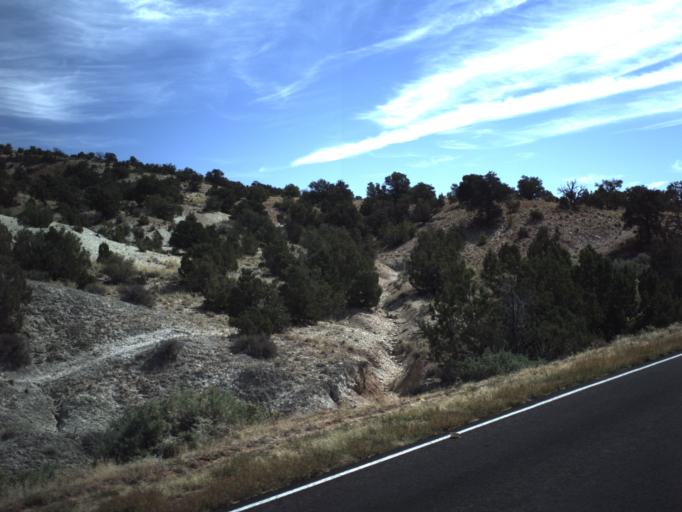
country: US
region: Utah
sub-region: Wayne County
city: Loa
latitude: 37.7517
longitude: -111.5673
